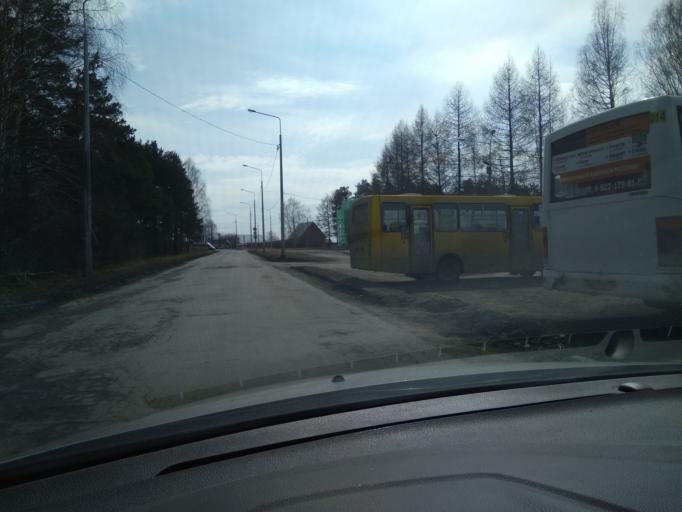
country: RU
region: Sverdlovsk
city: Shuvakish
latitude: 56.8936
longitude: 60.4850
